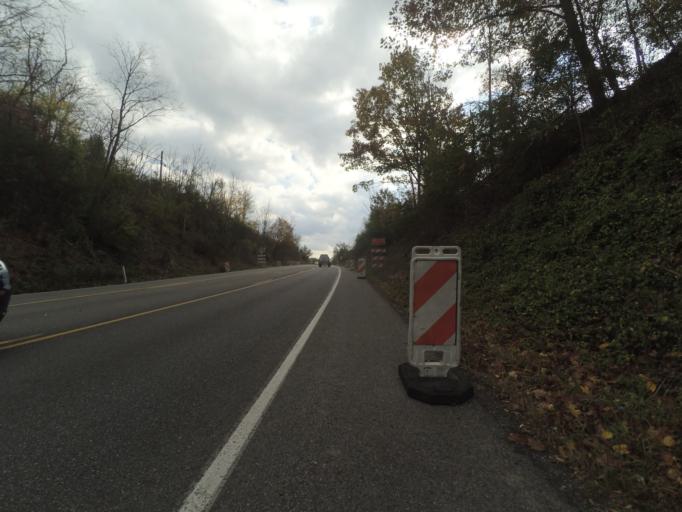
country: US
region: Pennsylvania
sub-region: Centre County
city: Bellefonte
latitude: 40.8994
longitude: -77.7898
